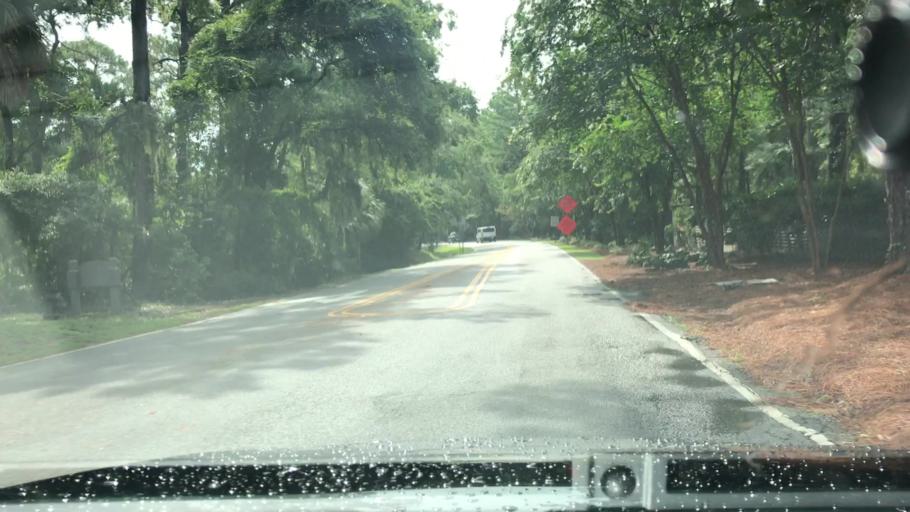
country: US
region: South Carolina
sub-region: Beaufort County
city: Hilton Head Island
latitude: 32.1347
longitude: -80.7733
